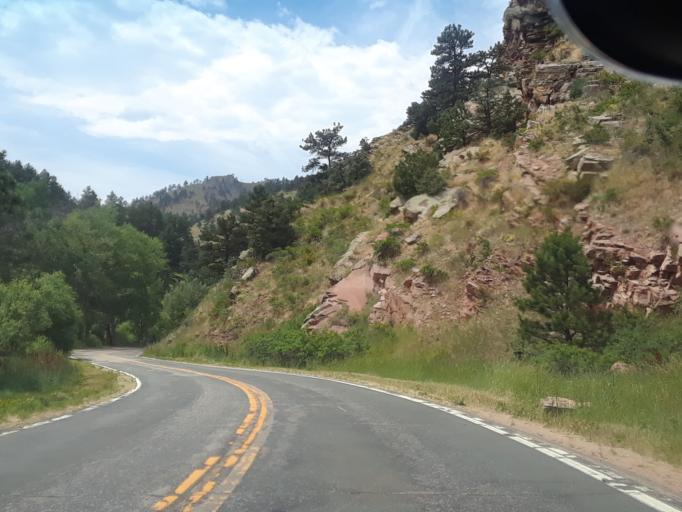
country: US
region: Colorado
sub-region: Boulder County
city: Boulder
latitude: 40.1090
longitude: -105.3029
